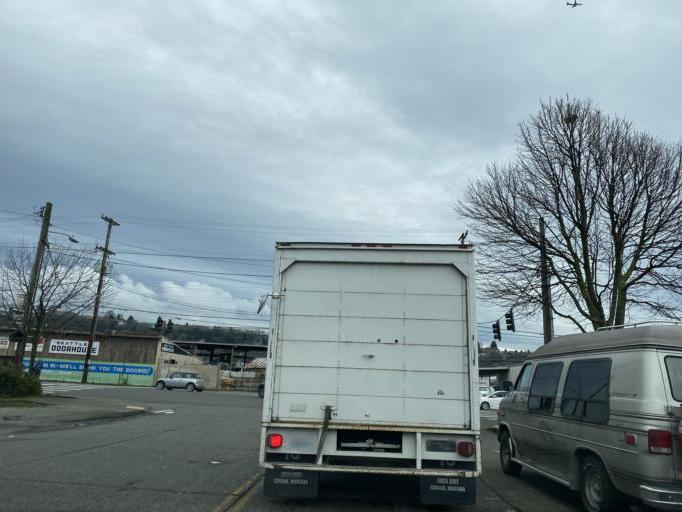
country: US
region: Washington
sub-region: King County
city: Seattle
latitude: 47.5819
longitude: -122.3297
